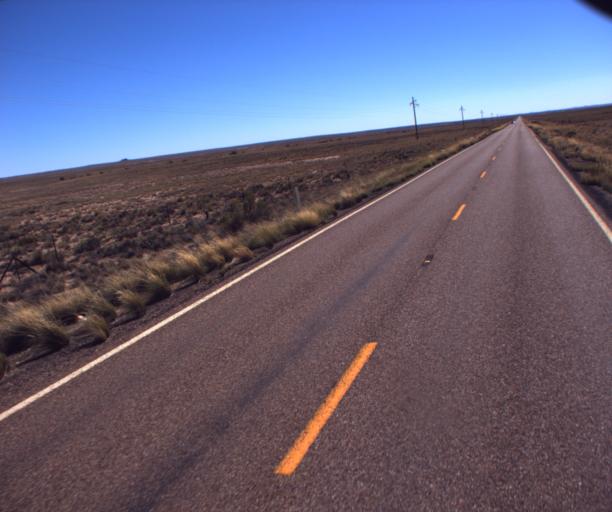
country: US
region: Arizona
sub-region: Navajo County
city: Holbrook
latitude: 35.1323
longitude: -110.0910
